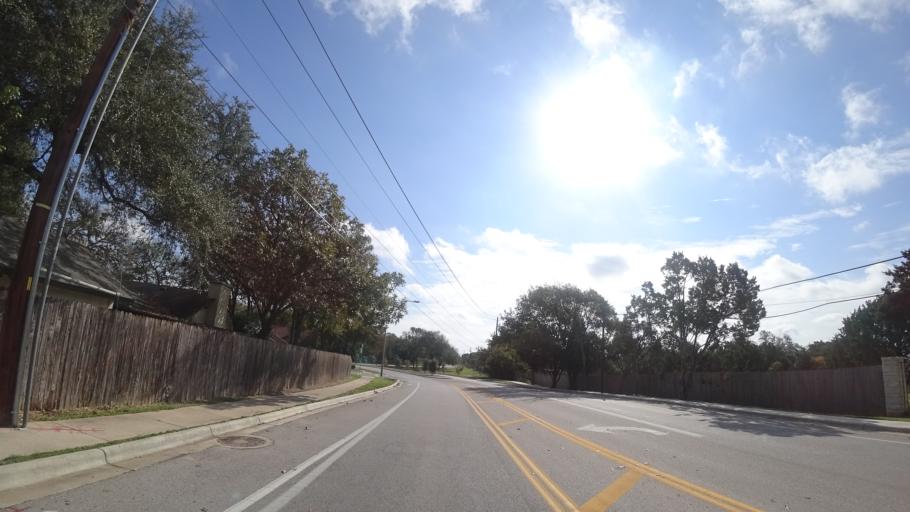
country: US
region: Texas
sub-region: Travis County
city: Shady Hollow
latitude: 30.1902
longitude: -97.8318
